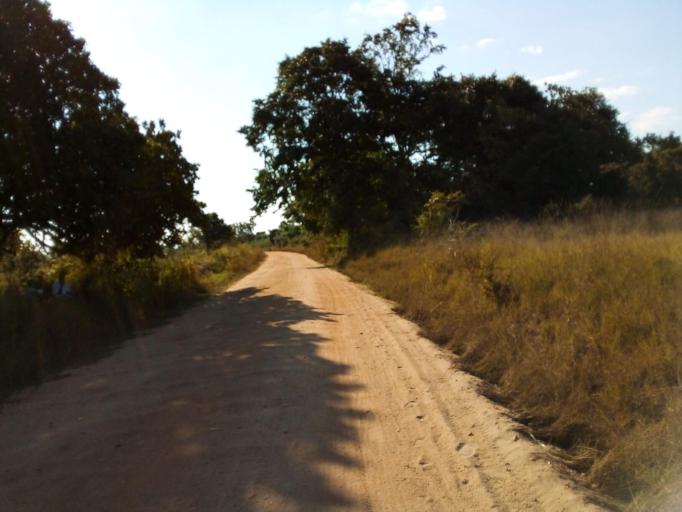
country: MZ
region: Zambezia
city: Quelimane
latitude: -17.5438
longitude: 36.6270
